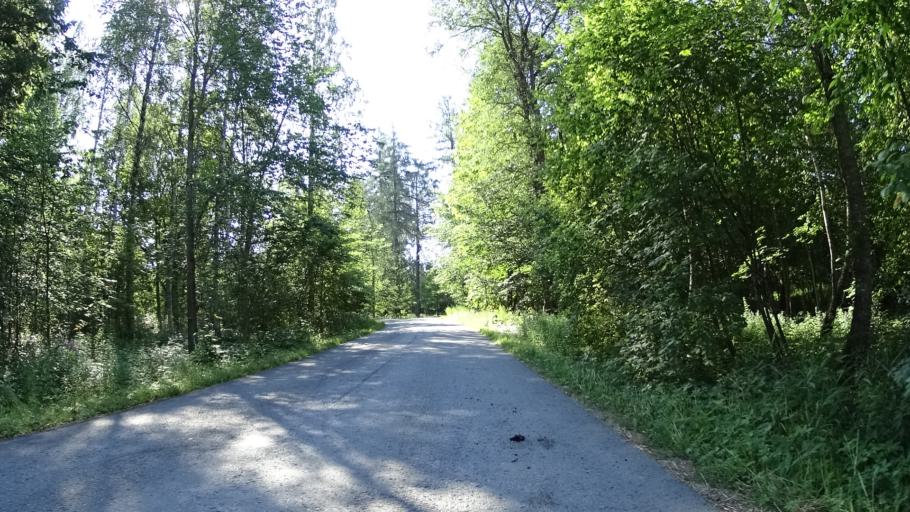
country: FI
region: Haeme
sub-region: Haemeenlinna
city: Haemeenlinna
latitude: 61.0269
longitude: 24.4483
